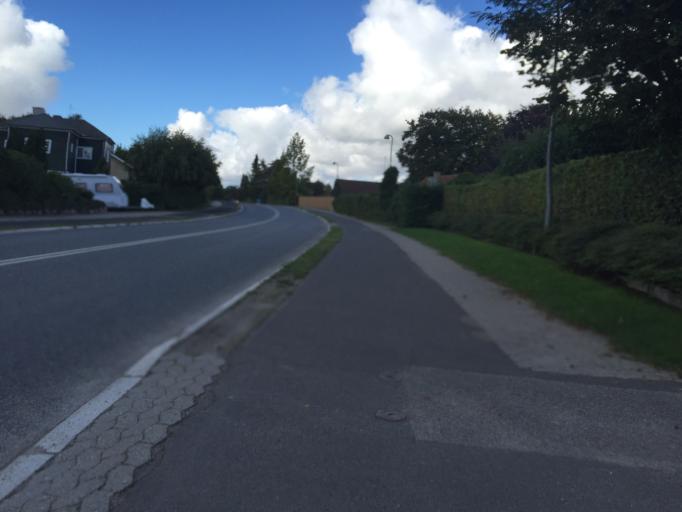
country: DK
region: Capital Region
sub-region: Fureso Kommune
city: Vaerlose
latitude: 55.7731
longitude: 12.3862
